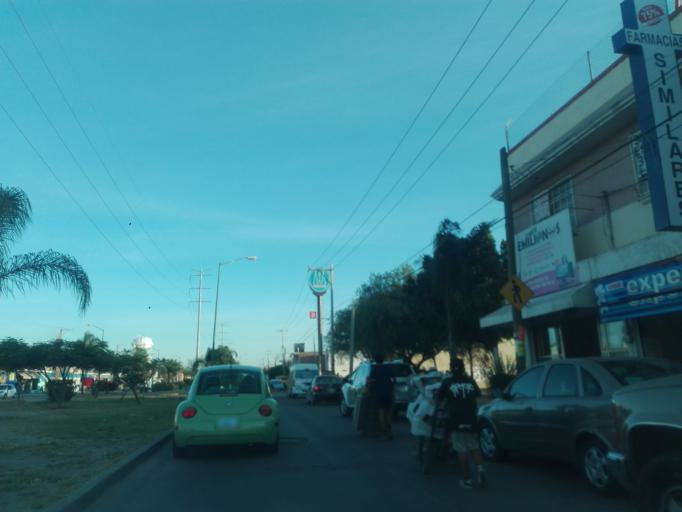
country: MX
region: Guanajuato
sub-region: Leon
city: Fraccionamiento Paraiso Real
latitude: 21.0791
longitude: -101.6211
